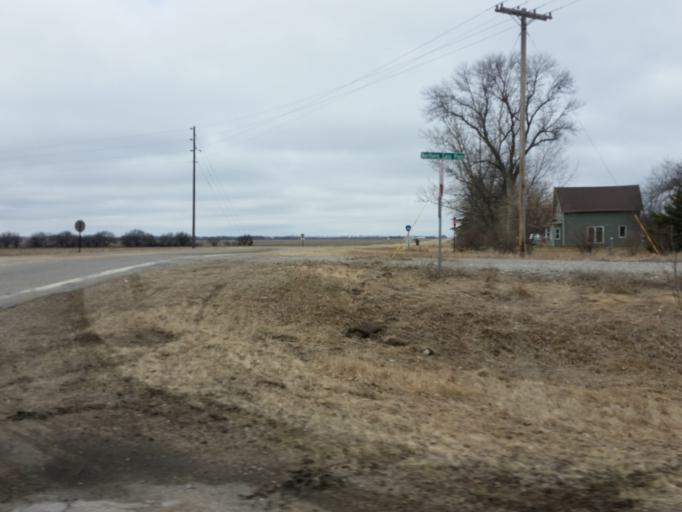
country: US
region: North Dakota
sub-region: Cass County
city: Casselton
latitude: 47.1081
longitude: -97.2181
